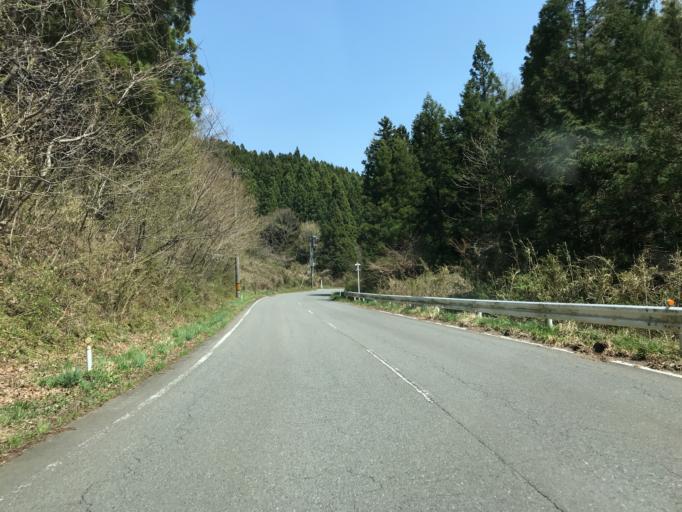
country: JP
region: Ibaraki
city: Kitaibaraki
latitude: 36.9769
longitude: 140.6286
